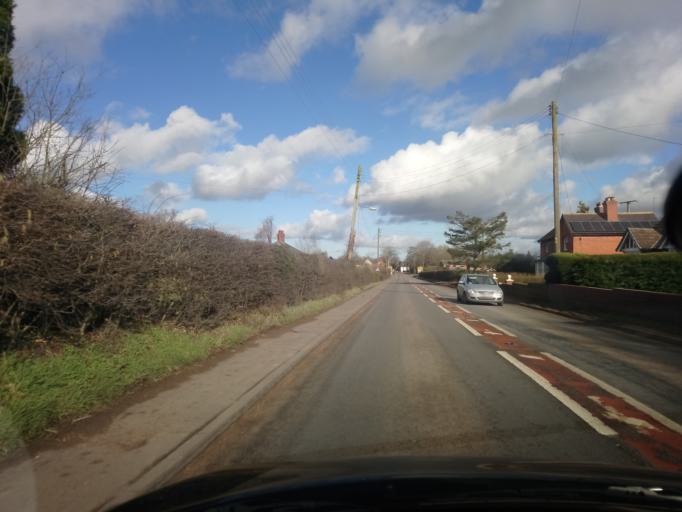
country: GB
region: England
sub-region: Shropshire
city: Astley
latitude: 52.7707
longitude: -2.7123
